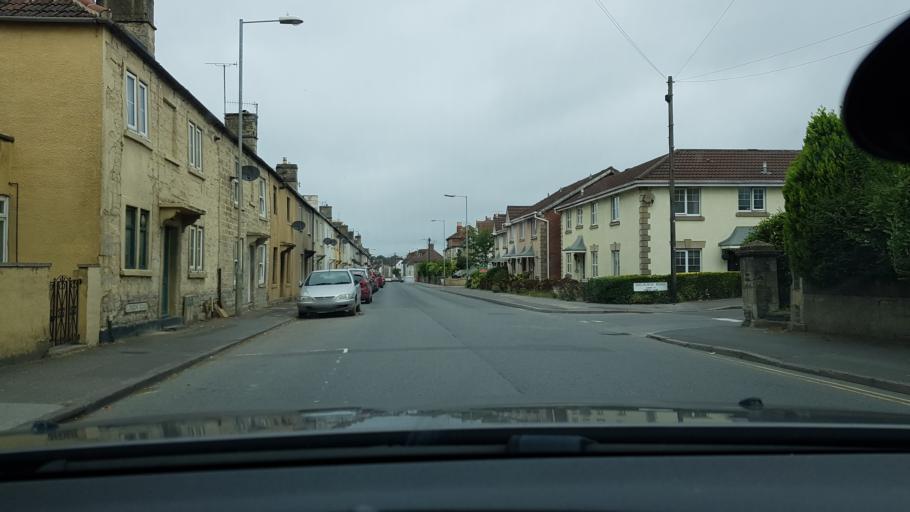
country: GB
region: England
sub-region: Wiltshire
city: Calne
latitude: 51.4322
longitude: -1.9999
